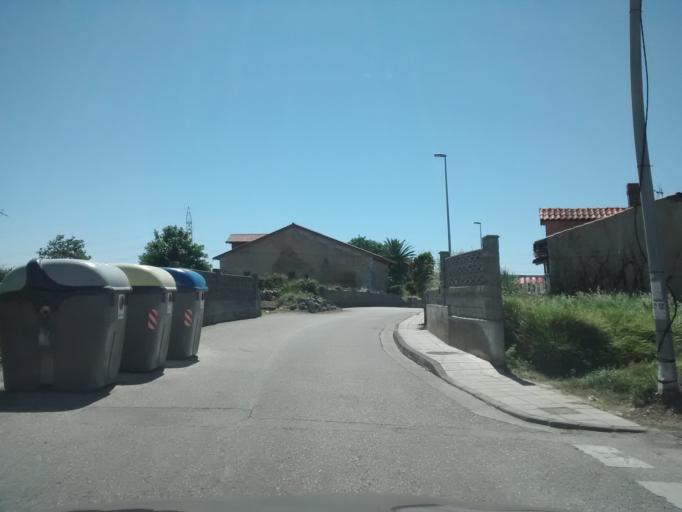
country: ES
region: Cantabria
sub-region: Provincia de Cantabria
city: Santander
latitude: 43.4779
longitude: -3.8138
